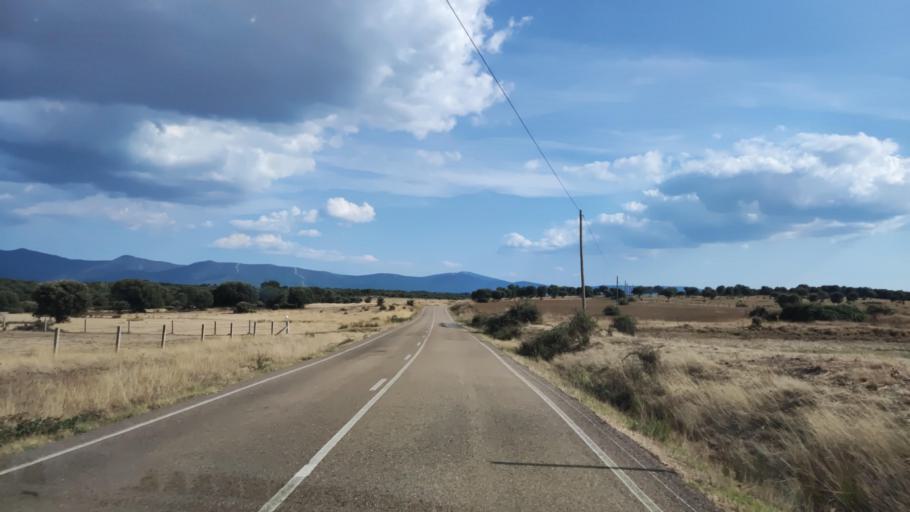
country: ES
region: Castille and Leon
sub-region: Provincia de Salamanca
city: Martiago
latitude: 40.4817
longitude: -6.4926
